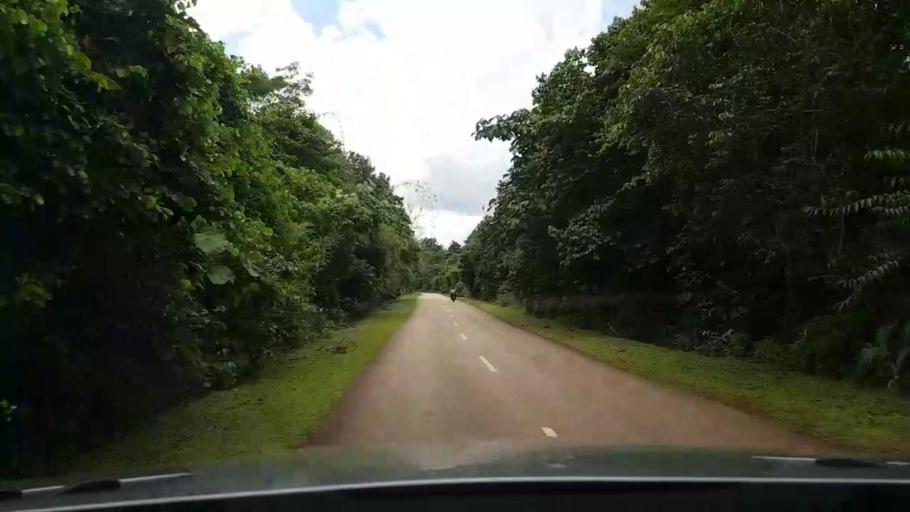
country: MY
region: Pahang
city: Pekan
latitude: 3.1279
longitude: 102.9751
